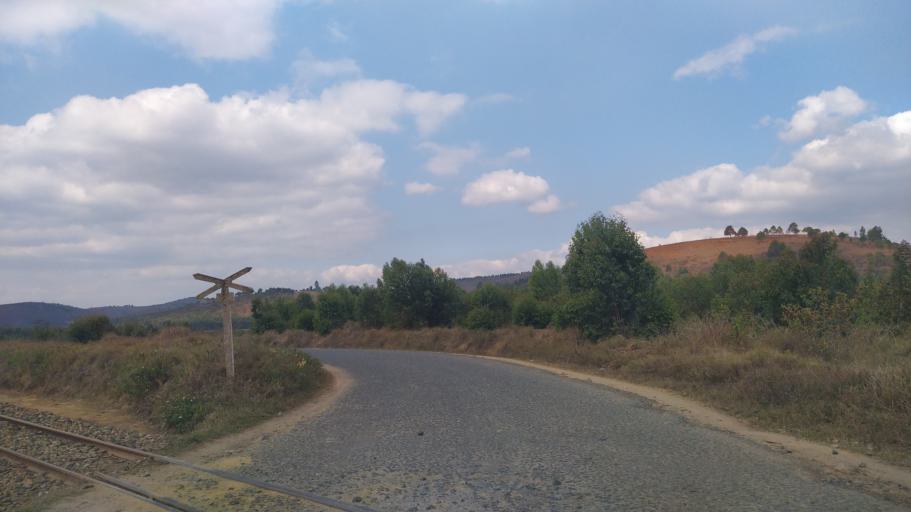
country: MG
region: Alaotra Mangoro
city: Moramanga
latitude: -18.7677
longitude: 48.2531
